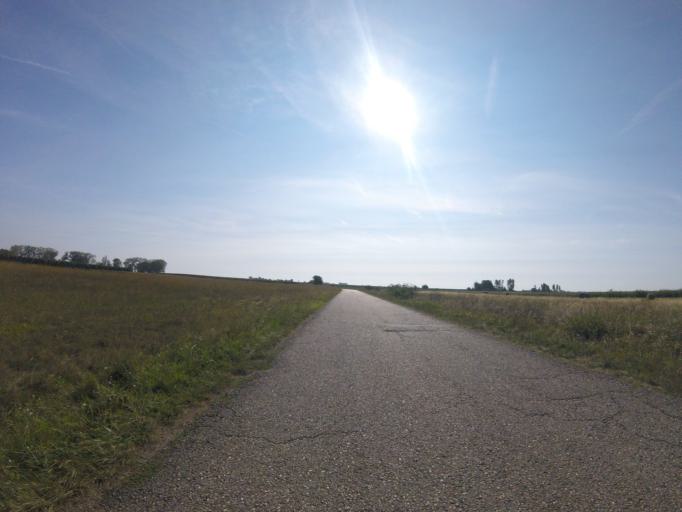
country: AT
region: Burgenland
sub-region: Politischer Bezirk Neusiedl am See
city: Illmitz
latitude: 47.7822
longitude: 16.8314
